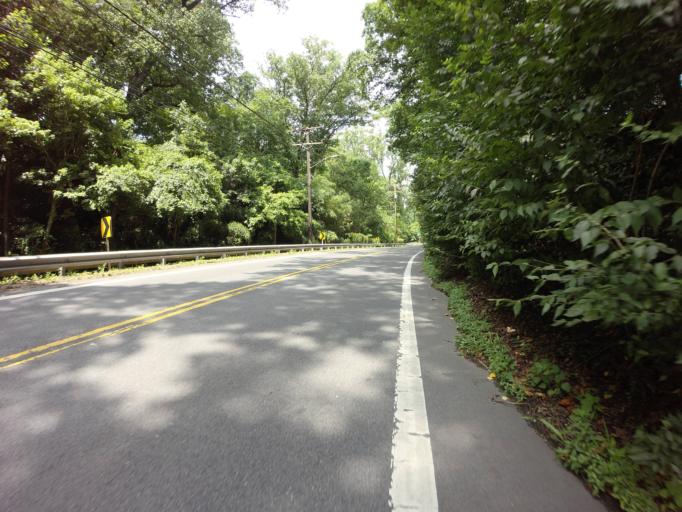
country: US
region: Maryland
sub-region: Montgomery County
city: Kensington
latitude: 39.0320
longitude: -77.0876
